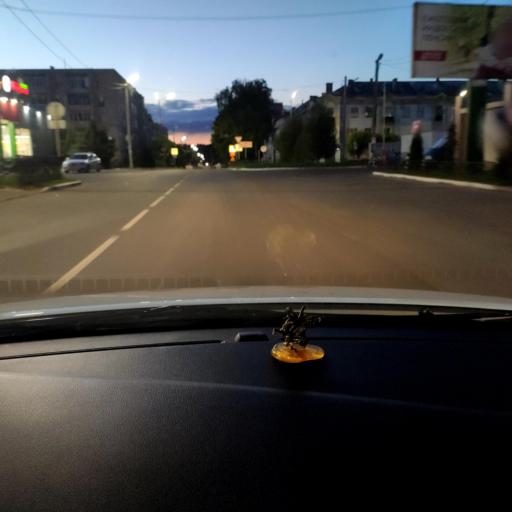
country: RU
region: Tatarstan
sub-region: Zelenodol'skiy Rayon
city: Zelenodolsk
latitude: 55.8502
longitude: 48.4986
